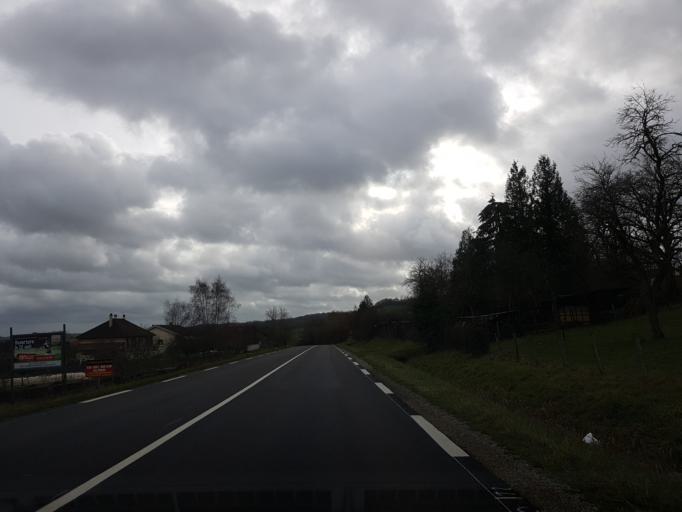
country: FR
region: Champagne-Ardenne
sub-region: Departement de la Haute-Marne
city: Langres
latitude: 47.8654
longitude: 5.3425
